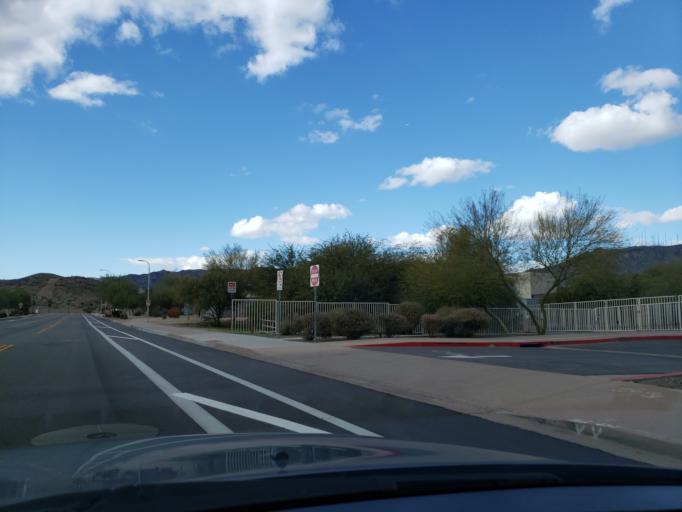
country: US
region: Arizona
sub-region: Maricopa County
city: Guadalupe
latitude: 33.2956
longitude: -112.0592
